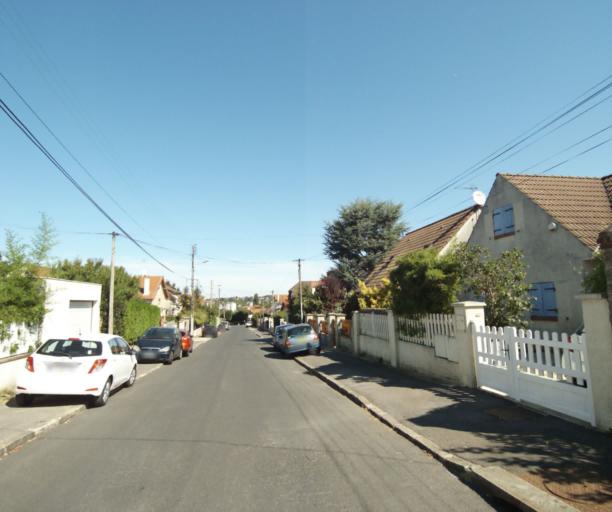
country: FR
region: Ile-de-France
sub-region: Departement de Seine-et-Marne
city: Lagny-sur-Marne
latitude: 48.8727
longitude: 2.7141
